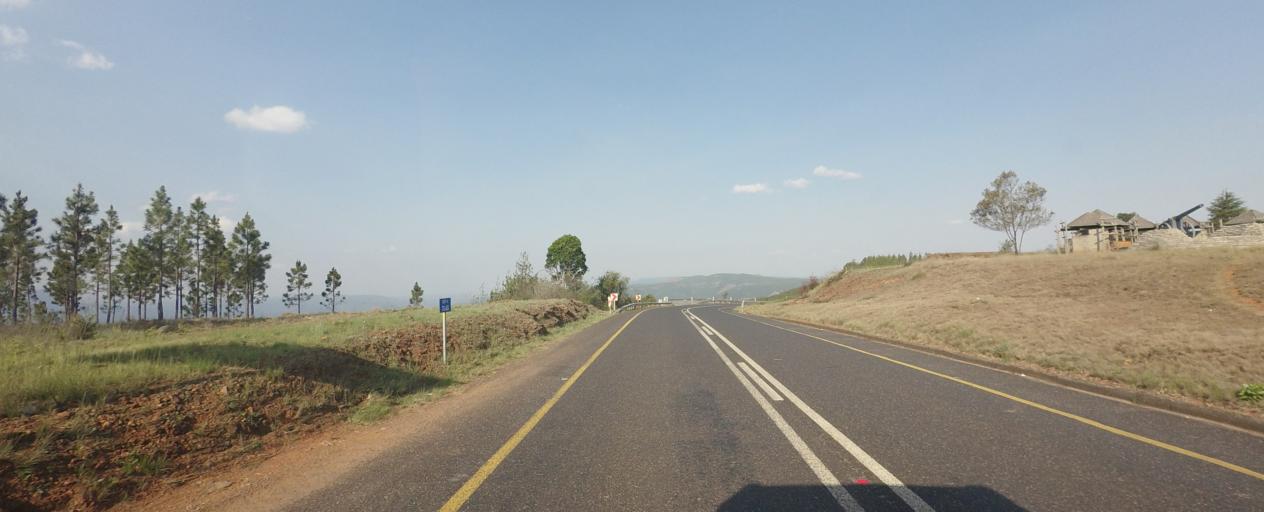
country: ZA
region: Mpumalanga
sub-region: Ehlanzeni District
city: Lydenburg
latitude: -25.1635
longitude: 30.6797
